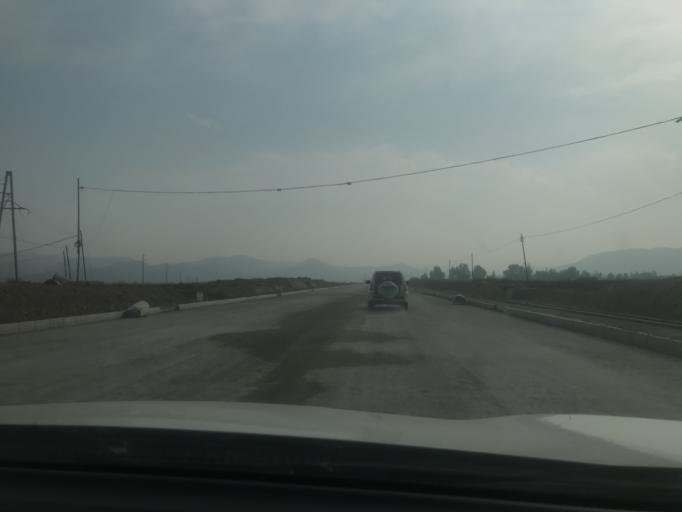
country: CN
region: Gansu Sheng
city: Gulang
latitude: 37.5068
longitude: 102.9012
